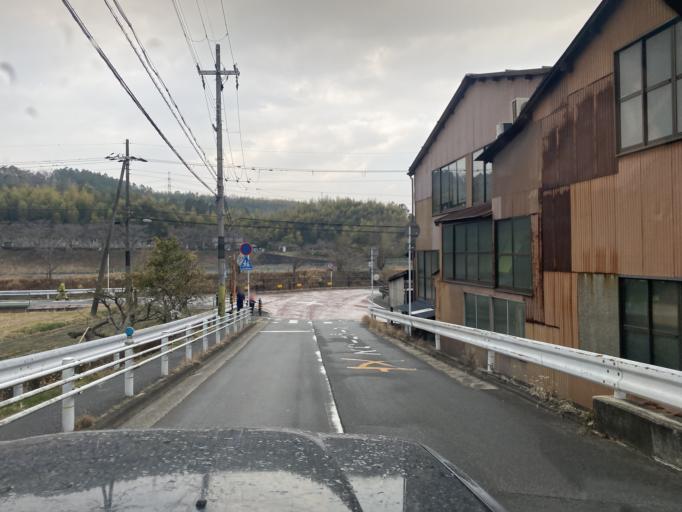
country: JP
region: Kyoto
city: Tanabe
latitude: 34.8213
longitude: 135.7542
